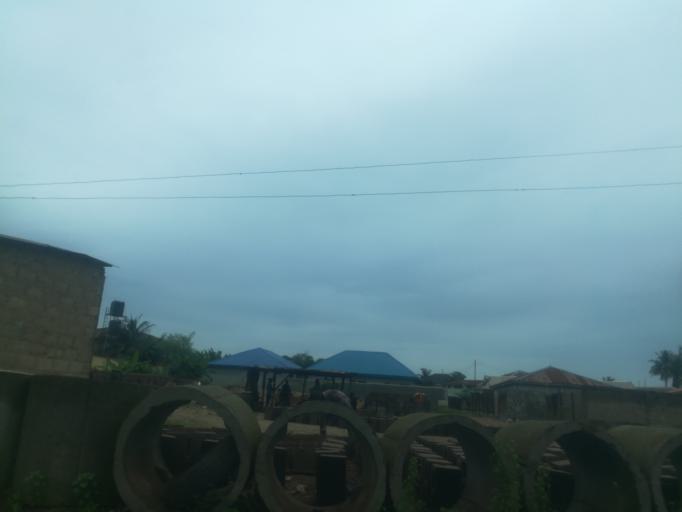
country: NG
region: Oyo
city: Ibadan
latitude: 7.3278
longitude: 3.8905
